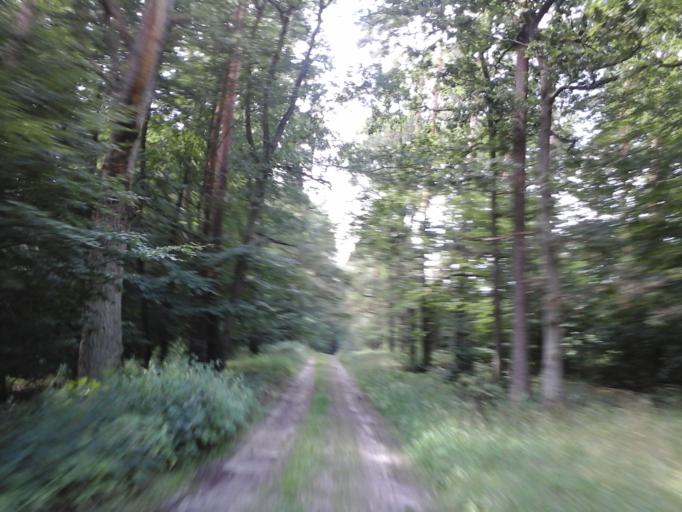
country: PL
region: West Pomeranian Voivodeship
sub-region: Powiat choszczenski
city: Bierzwnik
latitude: 53.0801
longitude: 15.6551
